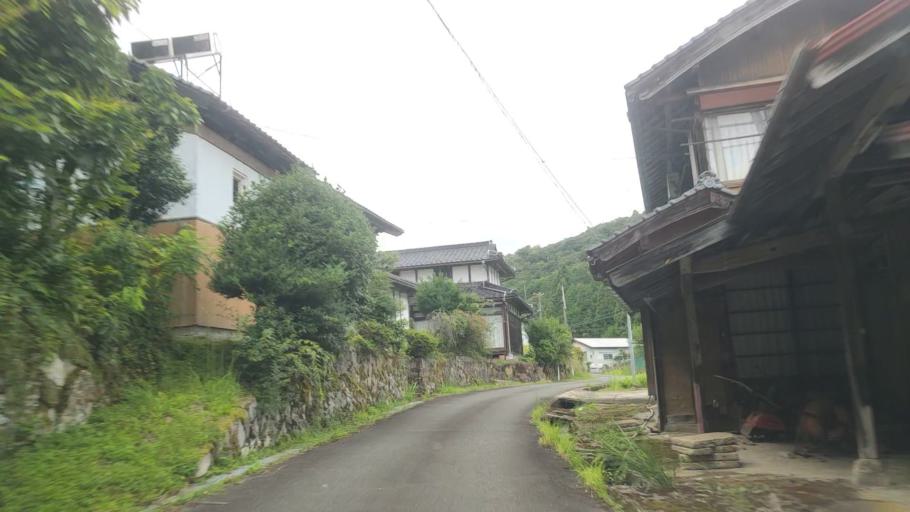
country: JP
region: Hyogo
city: Toyooka
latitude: 35.6002
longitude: 134.8802
